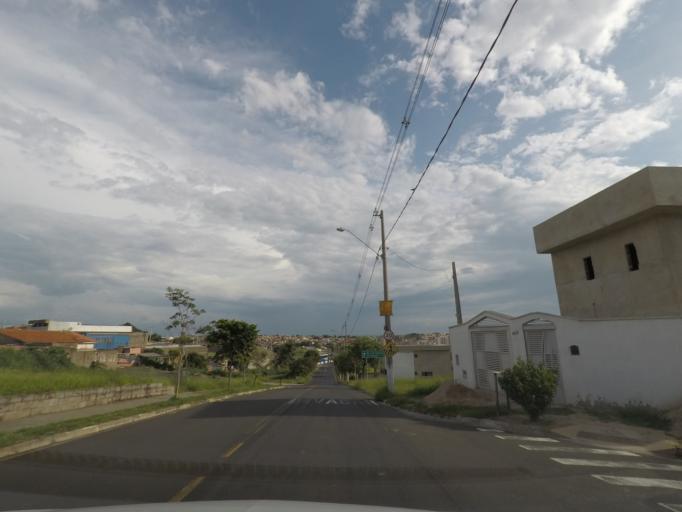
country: BR
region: Sao Paulo
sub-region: Campinas
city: Campinas
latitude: -22.9192
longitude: -47.1158
